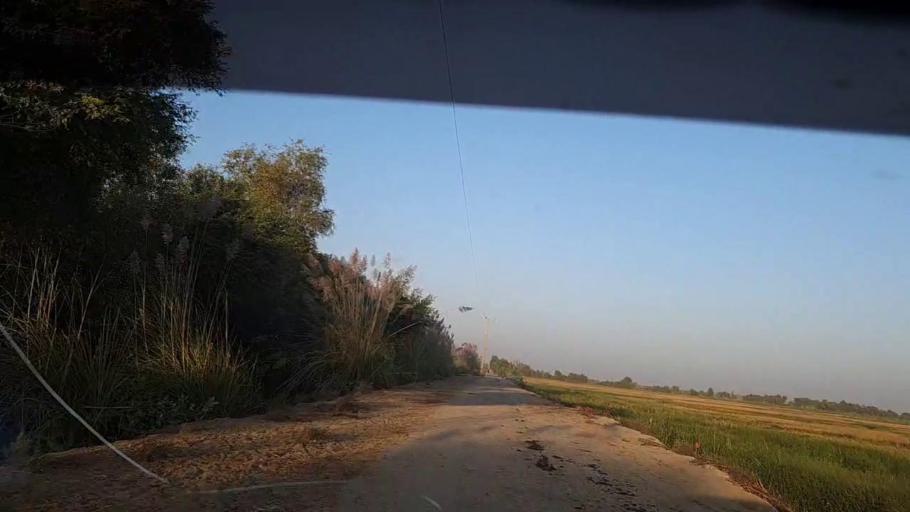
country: PK
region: Sindh
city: Ratodero
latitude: 27.8889
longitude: 68.2173
